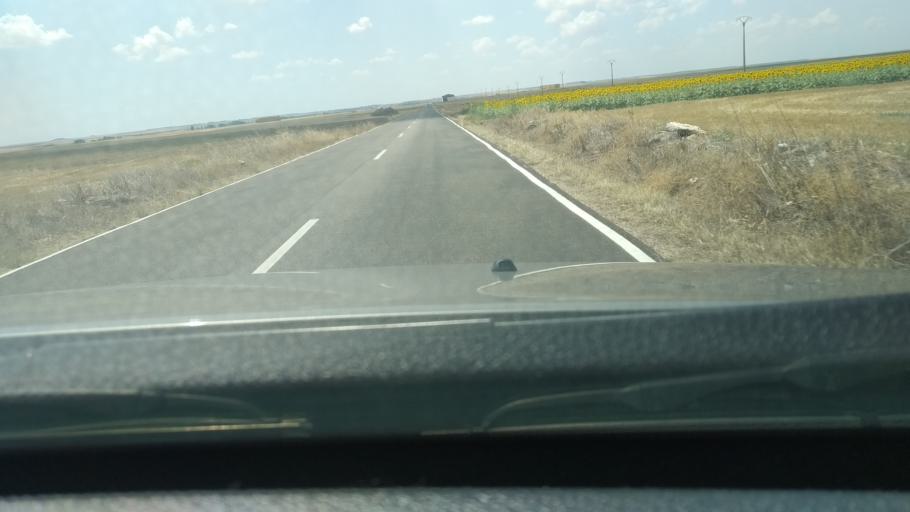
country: ES
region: Castille and Leon
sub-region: Provincia de Burgos
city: Villafruela
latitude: 41.9362
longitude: -3.8780
